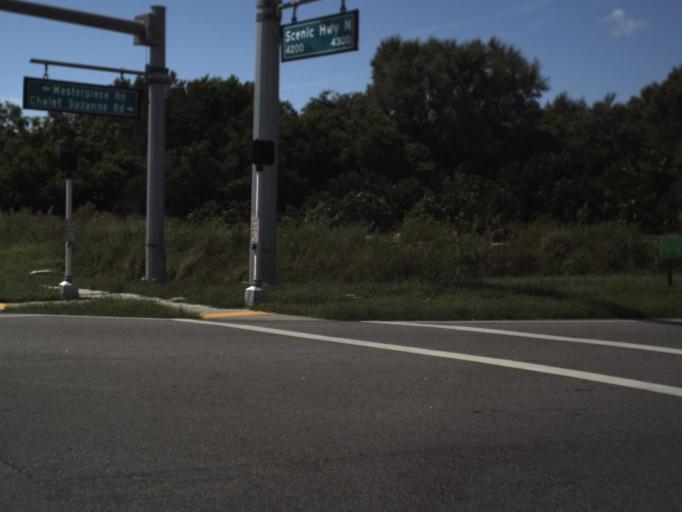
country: US
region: Florida
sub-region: Polk County
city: Lake Wales
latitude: 27.9595
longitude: -81.5948
